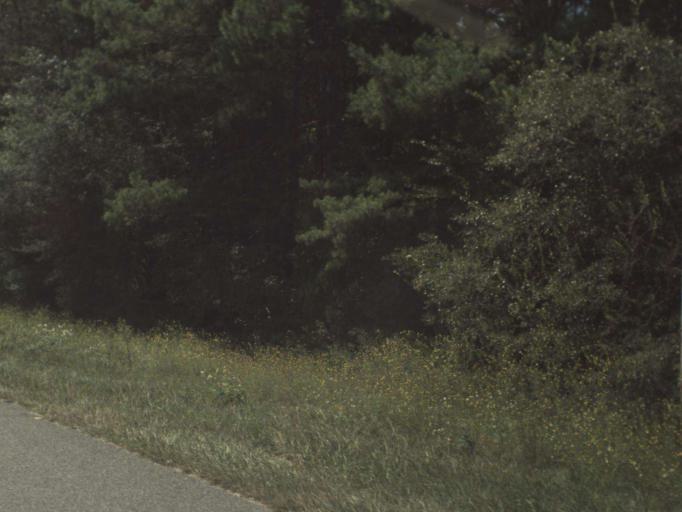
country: US
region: Florida
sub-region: Bay County
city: Youngstown
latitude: 30.5126
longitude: -85.6575
